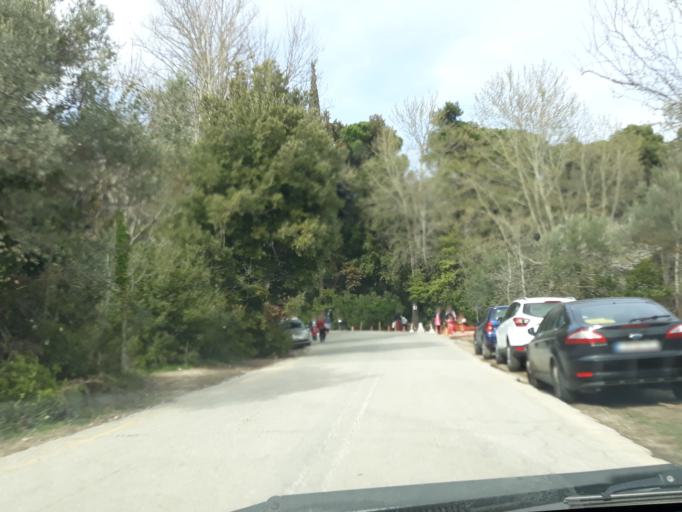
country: GR
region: Attica
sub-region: Nomarchia Anatolikis Attikis
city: Varybobi
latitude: 38.1602
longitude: 23.7923
